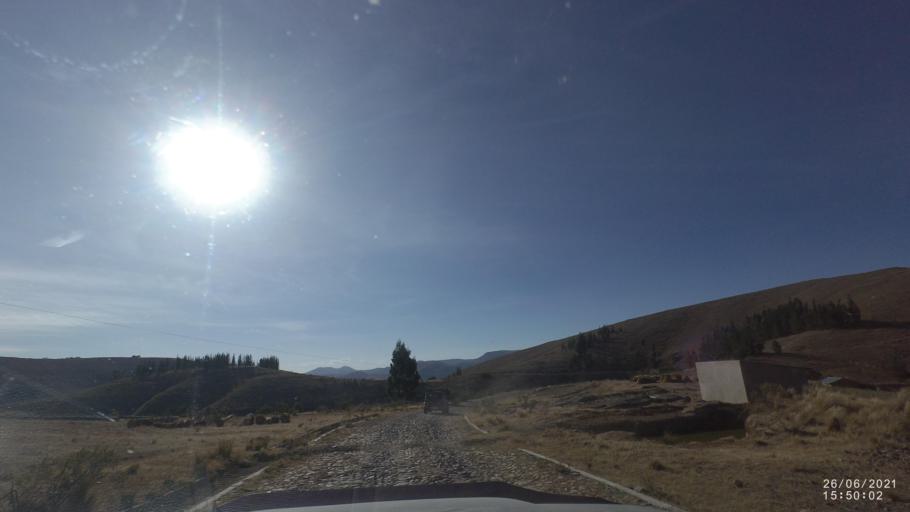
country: BO
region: Cochabamba
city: Arani
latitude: -17.8523
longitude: -65.7007
